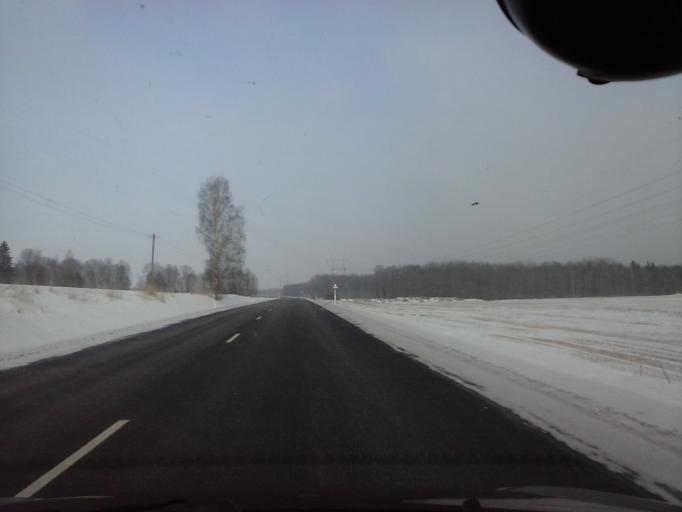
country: EE
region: Viljandimaa
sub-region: Abja vald
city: Abja-Paluoja
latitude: 58.2874
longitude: 25.2924
